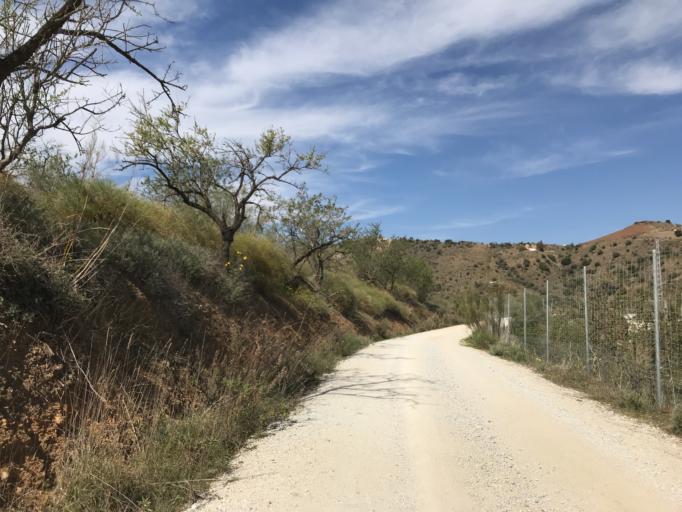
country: ES
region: Andalusia
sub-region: Provincia de Malaga
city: Valdes
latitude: 36.7762
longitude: -4.2179
